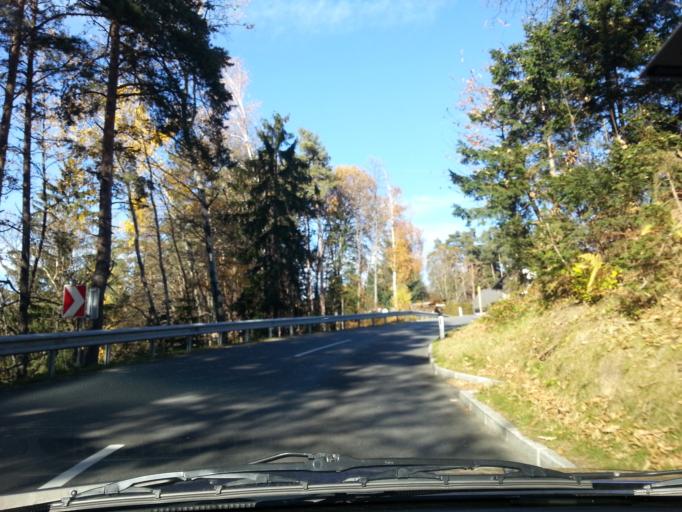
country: AT
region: Styria
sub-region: Politischer Bezirk Deutschlandsberg
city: Gundersdorf
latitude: 46.9506
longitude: 15.2312
